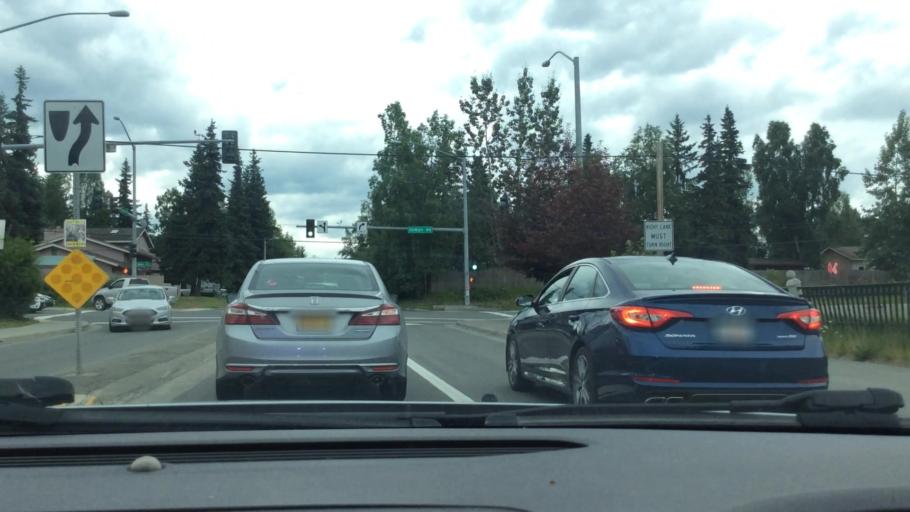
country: US
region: Alaska
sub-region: Anchorage Municipality
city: Elmendorf Air Force Base
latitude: 61.2102
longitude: -149.7559
